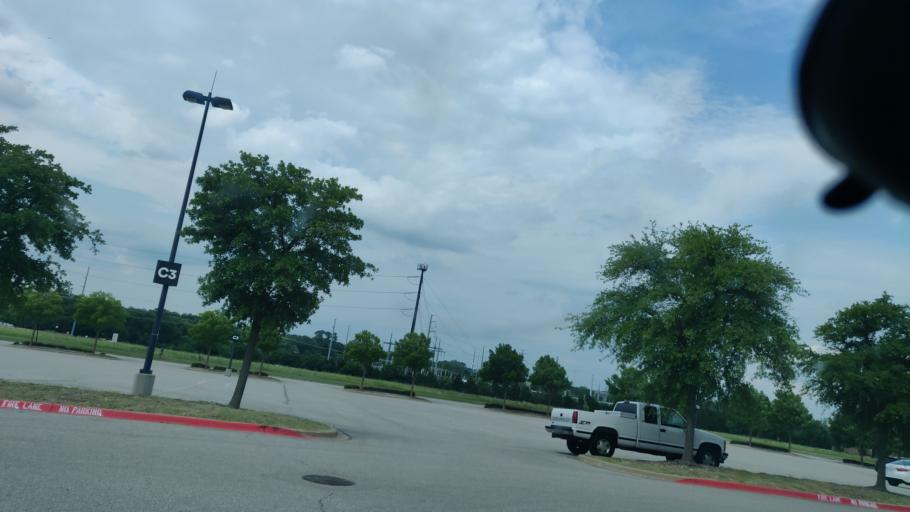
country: US
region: Texas
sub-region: Dallas County
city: Sachse
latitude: 32.9554
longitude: -96.6153
